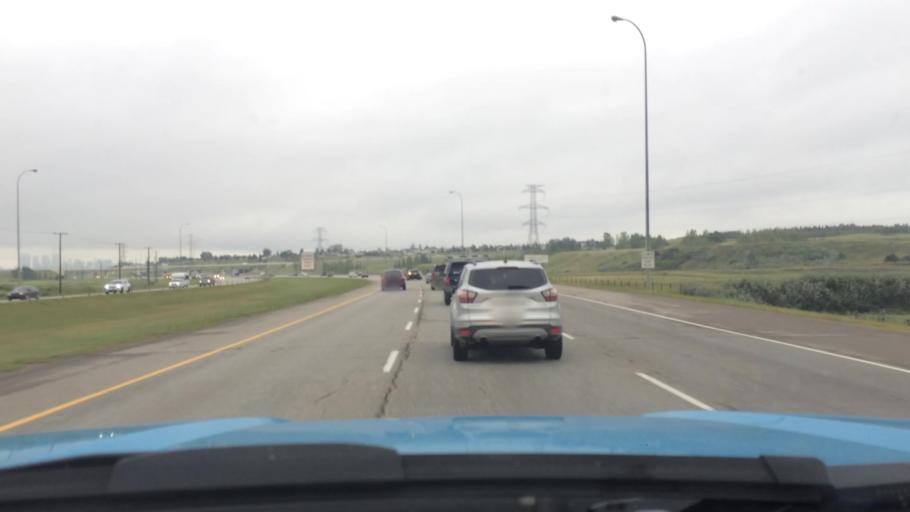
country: CA
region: Alberta
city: Calgary
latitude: 51.1338
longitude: -114.0432
